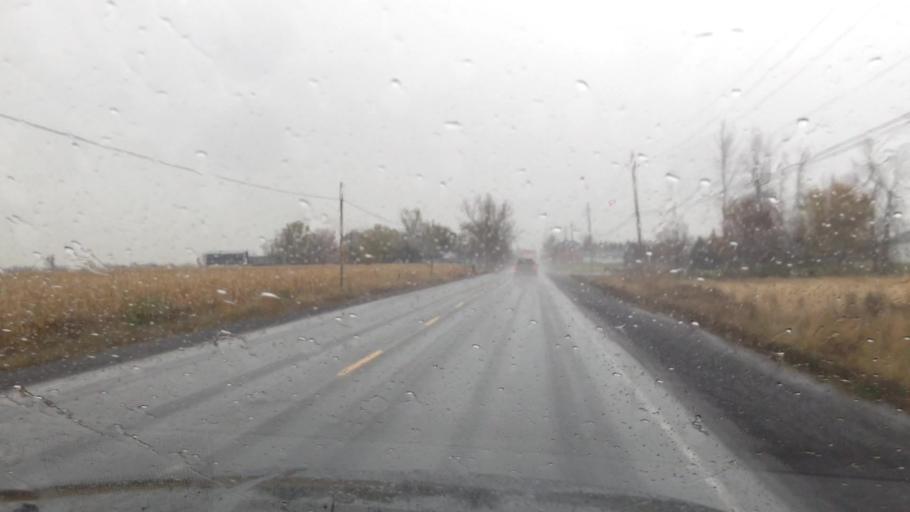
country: CA
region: Ontario
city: Bourget
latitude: 45.2955
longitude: -75.3256
